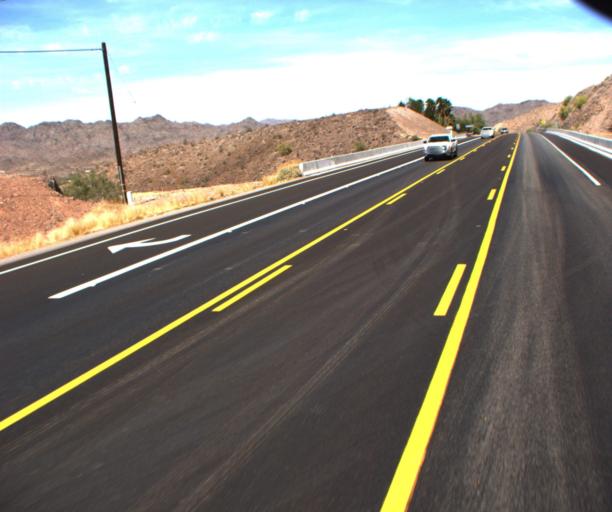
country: US
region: Arizona
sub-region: La Paz County
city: Cienega Springs
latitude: 34.2909
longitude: -114.1026
